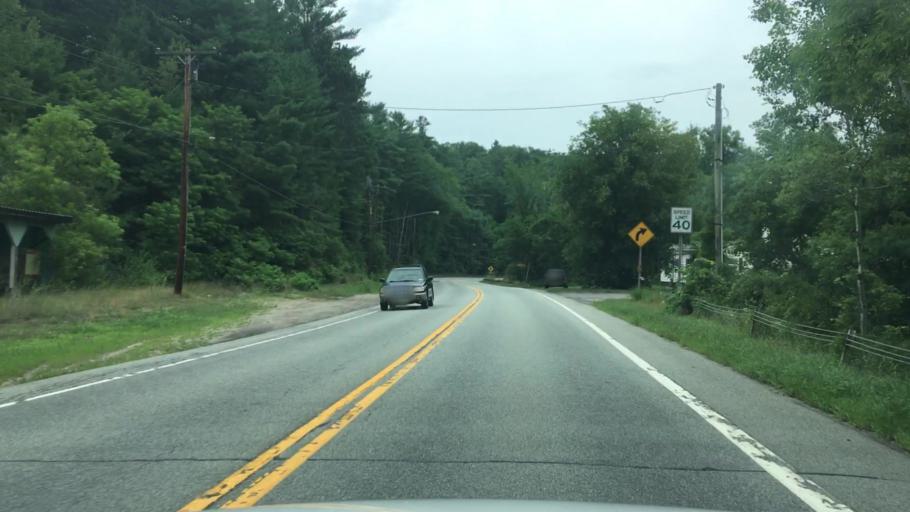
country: US
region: New York
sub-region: Clinton County
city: Peru
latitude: 44.4341
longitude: -73.6822
